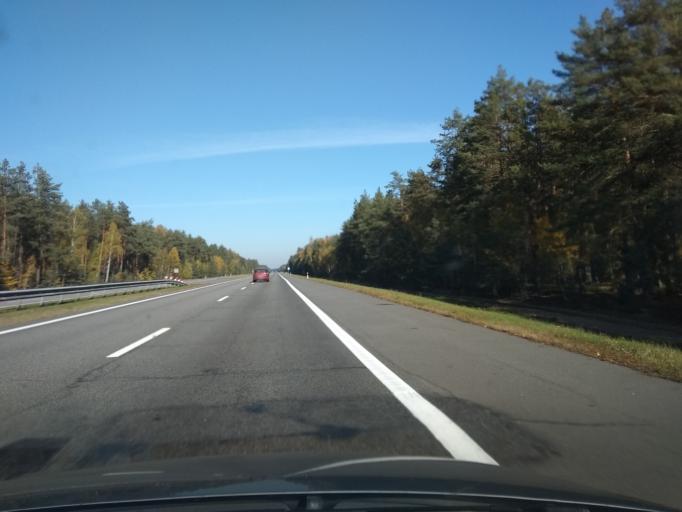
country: BY
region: Brest
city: Baranovichi
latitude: 52.9442
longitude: 25.7107
